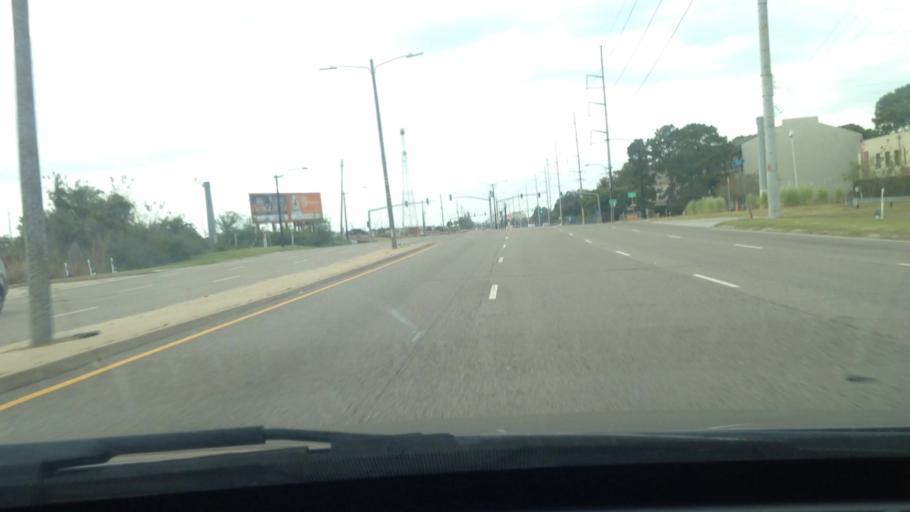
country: US
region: Louisiana
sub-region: Jefferson Parish
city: Jefferson
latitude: 29.9721
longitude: -90.1251
